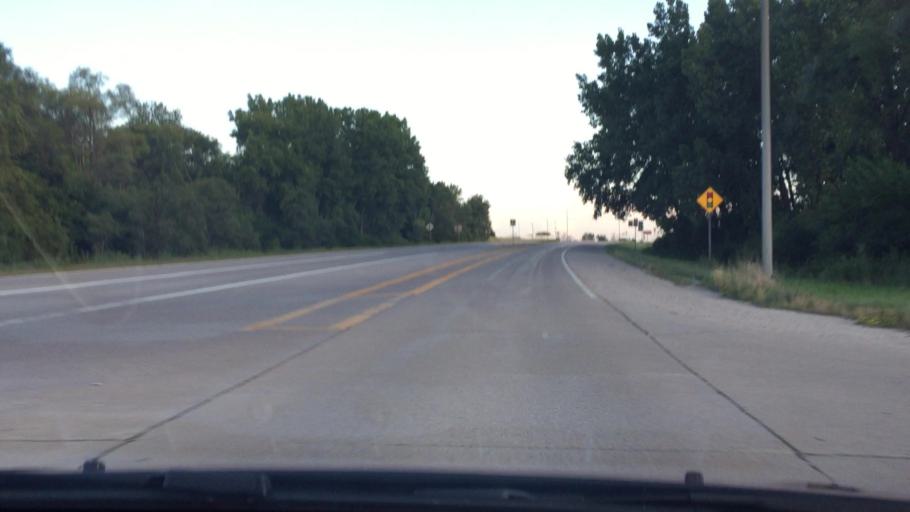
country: US
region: Iowa
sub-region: Muscatine County
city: Muscatine
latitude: 41.4581
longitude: -91.0306
